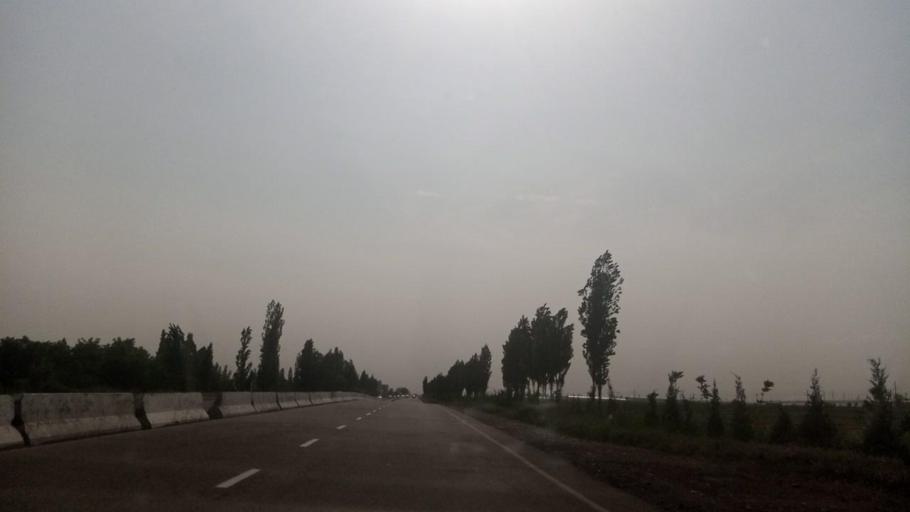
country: UZ
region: Toshkent
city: Ohangaron
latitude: 40.9130
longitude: 69.8218
